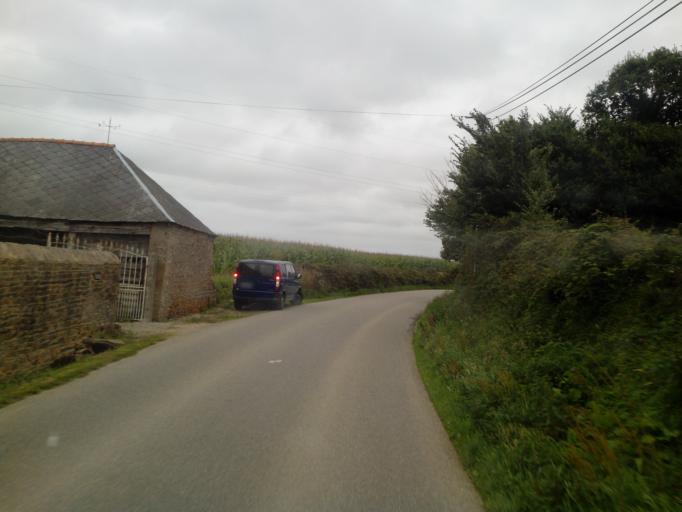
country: FR
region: Brittany
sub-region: Departement des Cotes-d'Armor
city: Plouha
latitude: 48.6807
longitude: -2.9538
